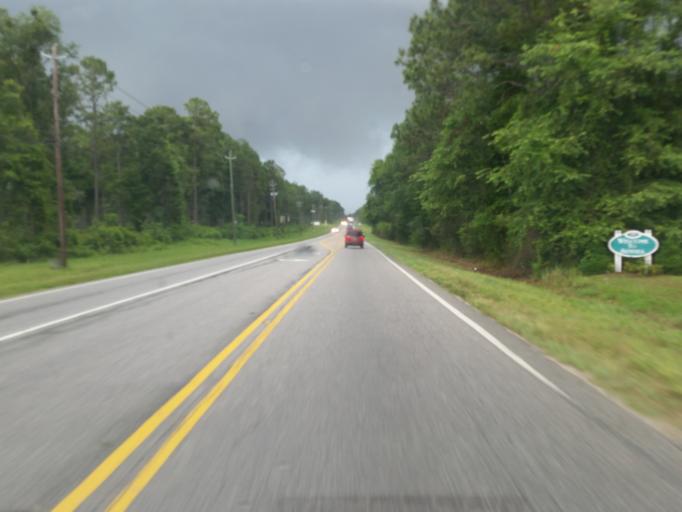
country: US
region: Alabama
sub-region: Mobile County
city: Chickasaw
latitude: 30.7891
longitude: -88.2931
